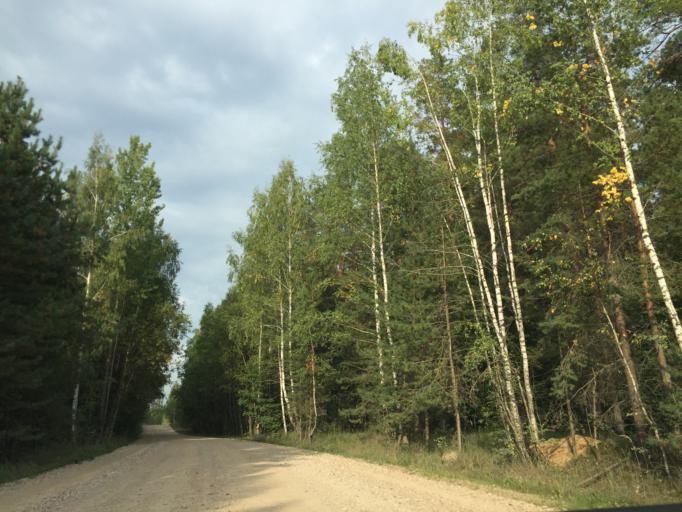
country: LV
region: Ikskile
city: Ikskile
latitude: 56.8081
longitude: 24.4443
